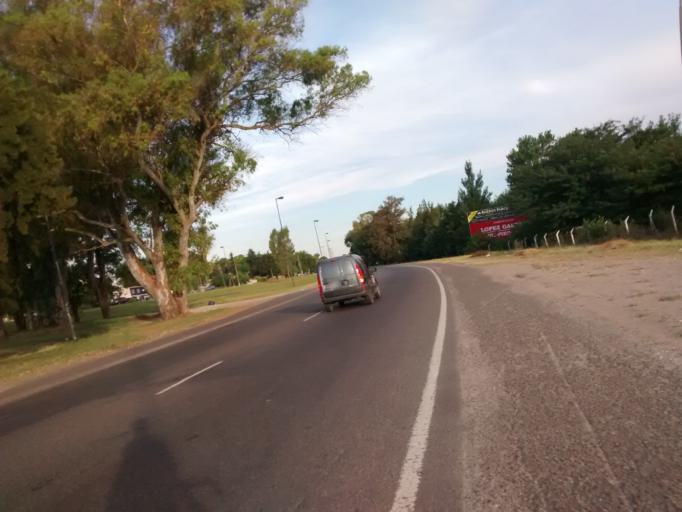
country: AR
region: Buenos Aires
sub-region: Partido de La Plata
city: La Plata
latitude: -34.8615
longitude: -58.0641
